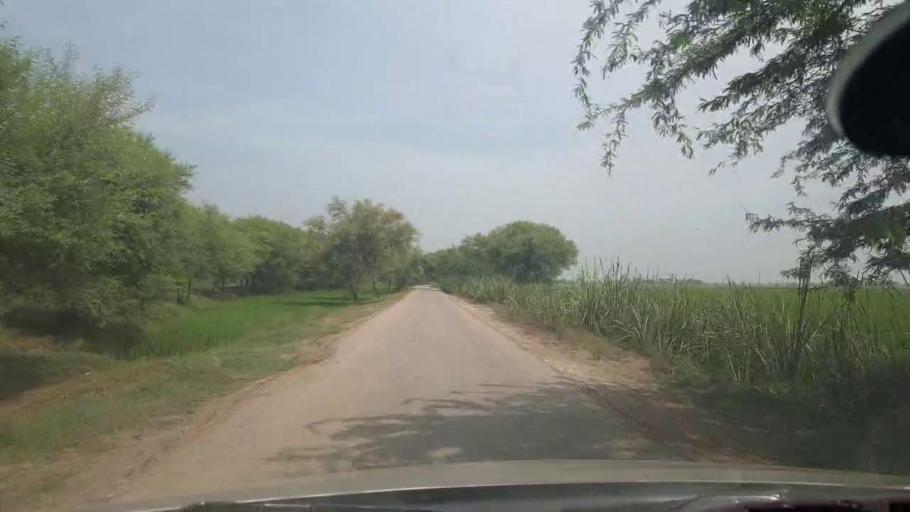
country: PK
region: Sindh
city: Jacobabad
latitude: 28.2999
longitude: 68.4758
